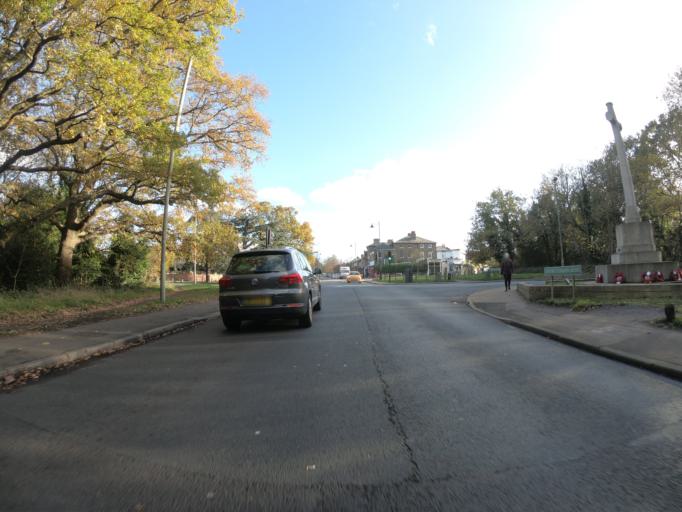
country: GB
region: England
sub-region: Greater London
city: Chislehurst
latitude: 51.4126
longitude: 0.0740
